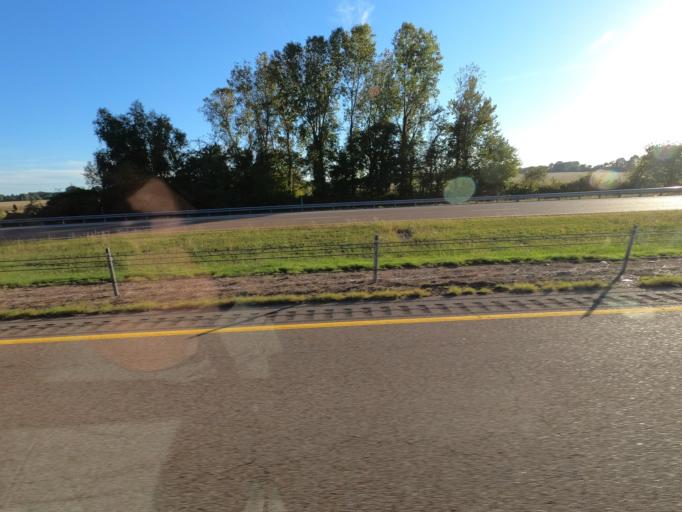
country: US
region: Tennessee
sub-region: Shelby County
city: Millington
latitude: 35.3112
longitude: -89.8579
